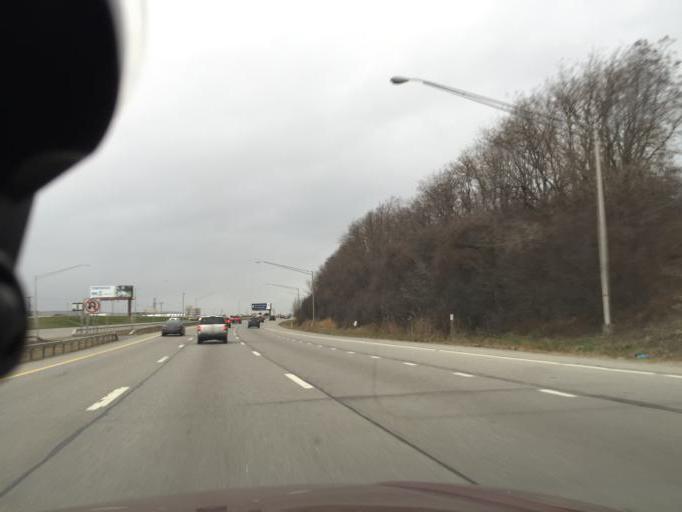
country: US
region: New York
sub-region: Monroe County
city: Rochester
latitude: 43.1252
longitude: -77.6538
